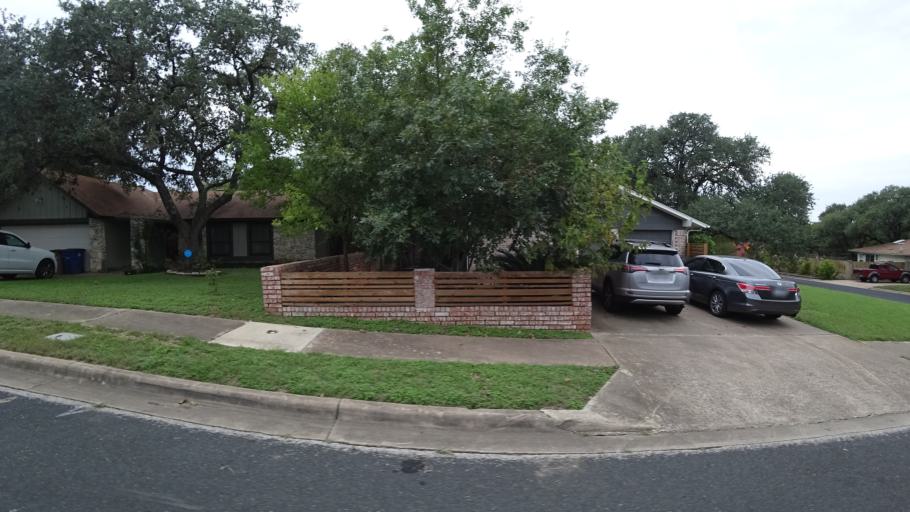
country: US
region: Texas
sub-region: Travis County
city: Rollingwood
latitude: 30.2121
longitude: -97.7862
